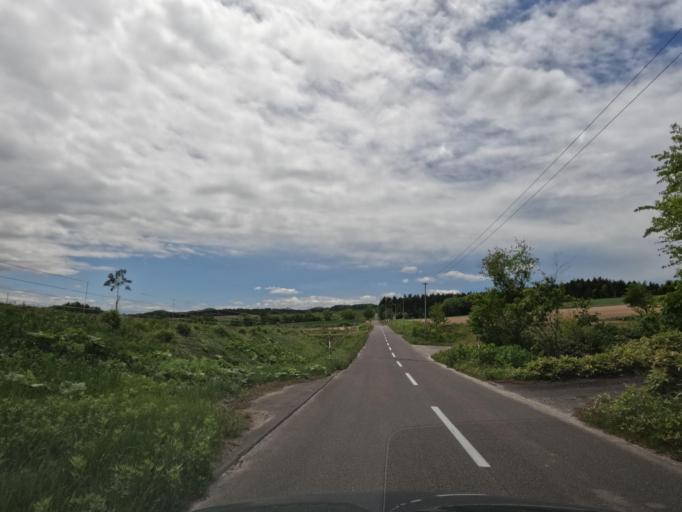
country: JP
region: Hokkaido
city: Shimo-furano
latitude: 43.5021
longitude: 142.4142
